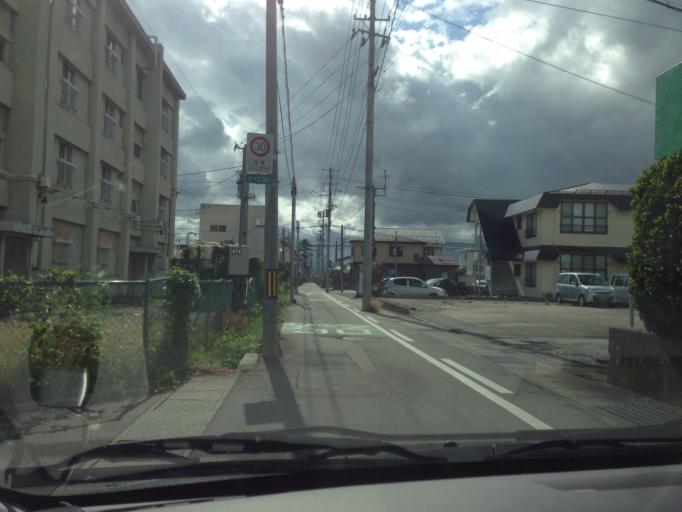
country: JP
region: Fukushima
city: Kitakata
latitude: 37.4922
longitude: 139.9335
